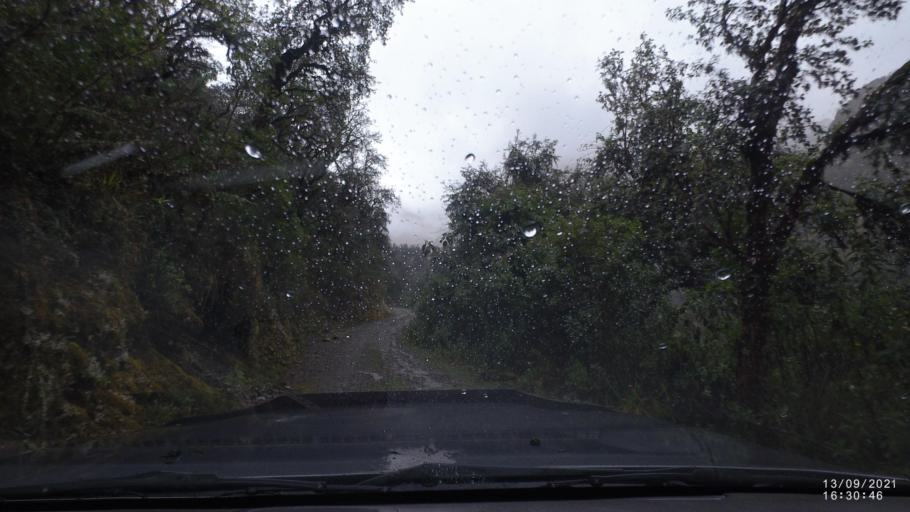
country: BO
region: Cochabamba
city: Colomi
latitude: -17.2748
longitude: -65.7116
